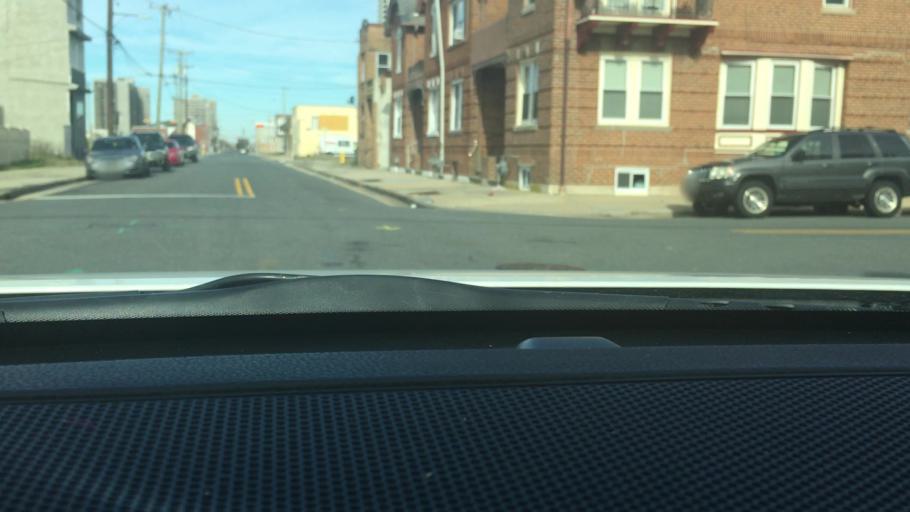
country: US
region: New Jersey
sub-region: Atlantic County
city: Atlantic City
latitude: 39.3655
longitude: -74.4112
